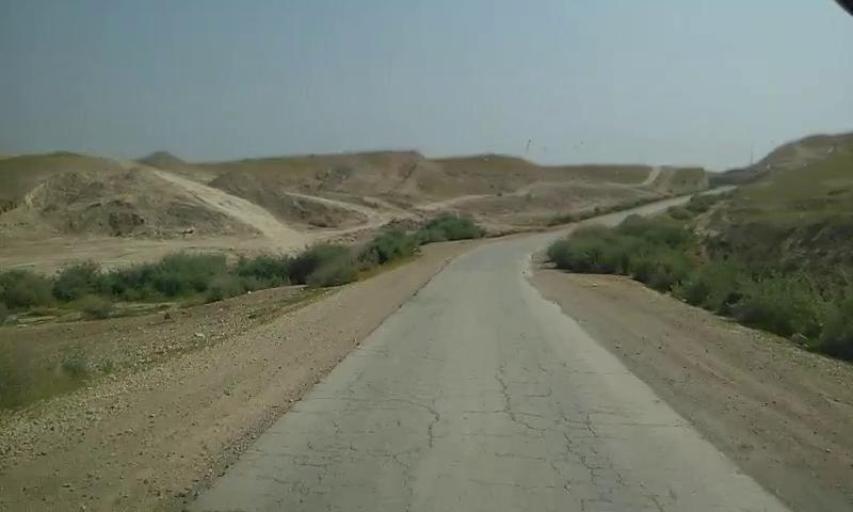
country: PS
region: West Bank
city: Jericho
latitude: 31.7947
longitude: 35.4271
